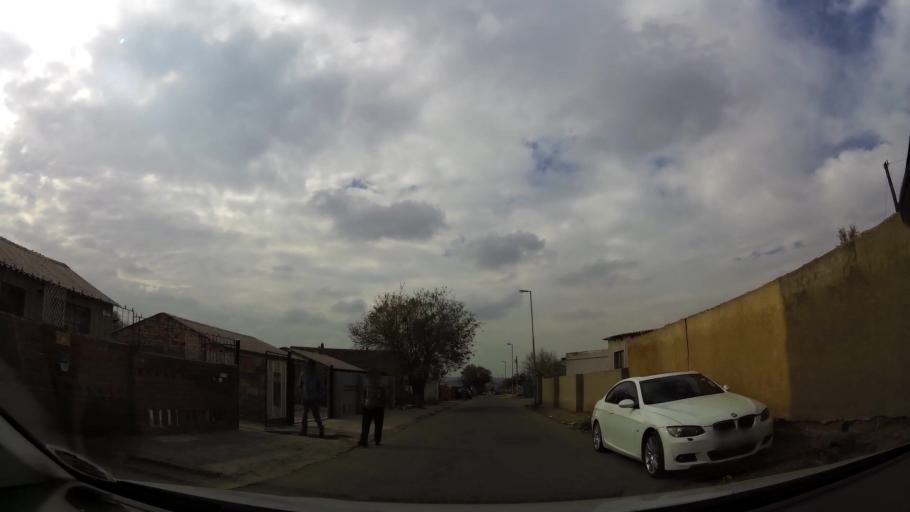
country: ZA
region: Gauteng
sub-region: City of Johannesburg Metropolitan Municipality
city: Soweto
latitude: -26.2710
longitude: 27.8619
